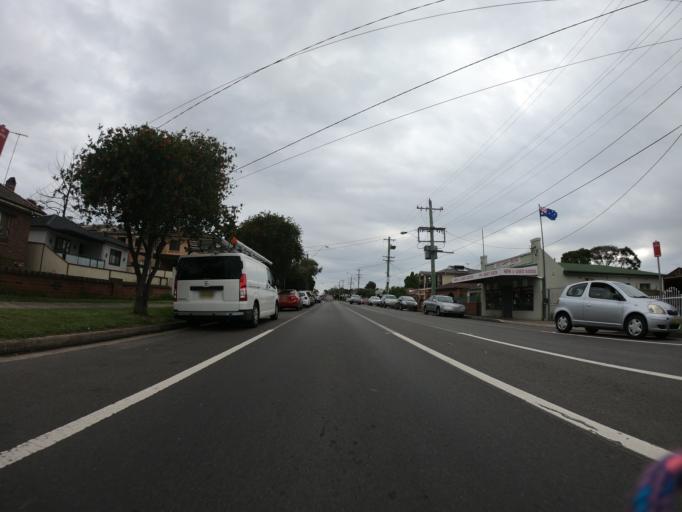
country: AU
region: New South Wales
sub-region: Parramatta
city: Granville
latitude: -33.8447
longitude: 151.0098
